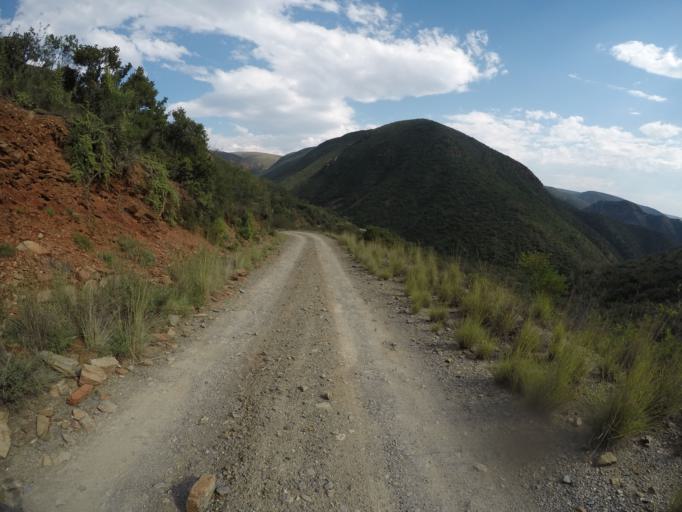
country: ZA
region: Eastern Cape
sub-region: Cacadu District Municipality
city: Kareedouw
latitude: -33.6477
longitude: 24.3388
